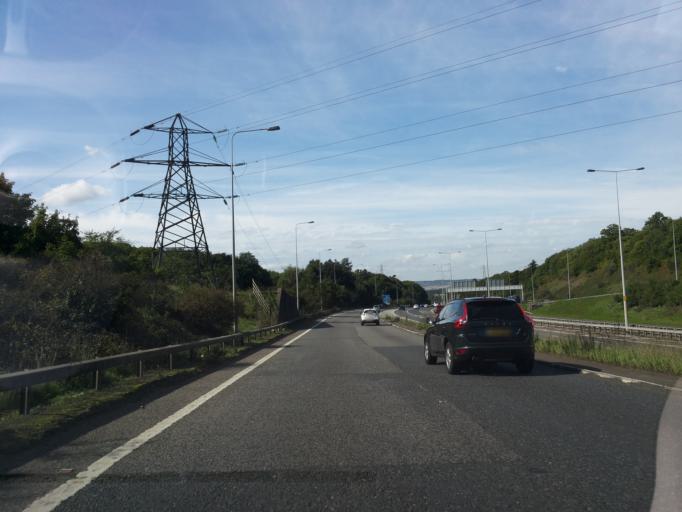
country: GB
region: England
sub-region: Kent
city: Boxley
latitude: 51.2877
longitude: 0.5482
